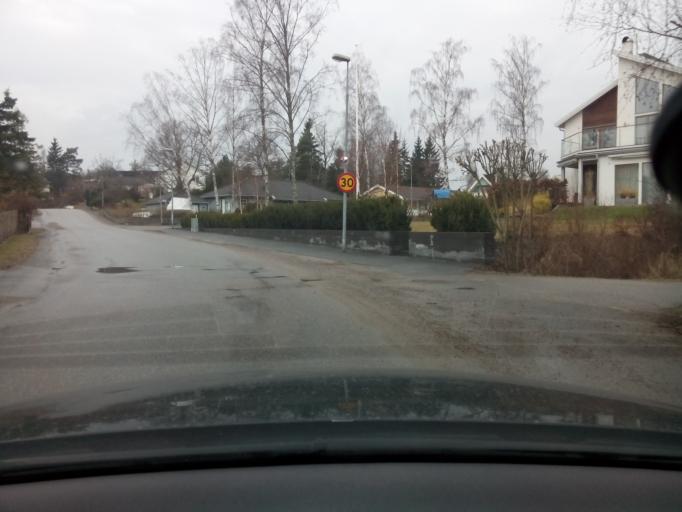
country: SE
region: Soedermanland
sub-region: Trosa Kommun
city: Trosa
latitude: 58.8943
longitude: 17.5649
